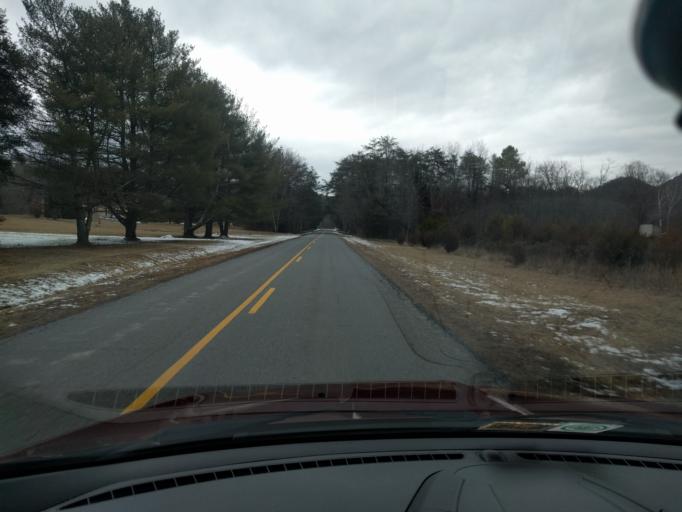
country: US
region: Virginia
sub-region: Alleghany County
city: Clifton Forge
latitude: 37.8207
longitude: -79.7410
